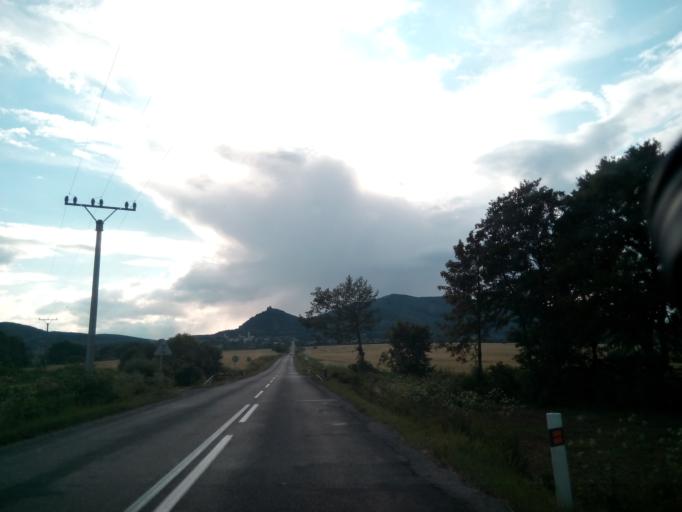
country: SK
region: Kosicky
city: Secovce
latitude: 48.6344
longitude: 21.5074
